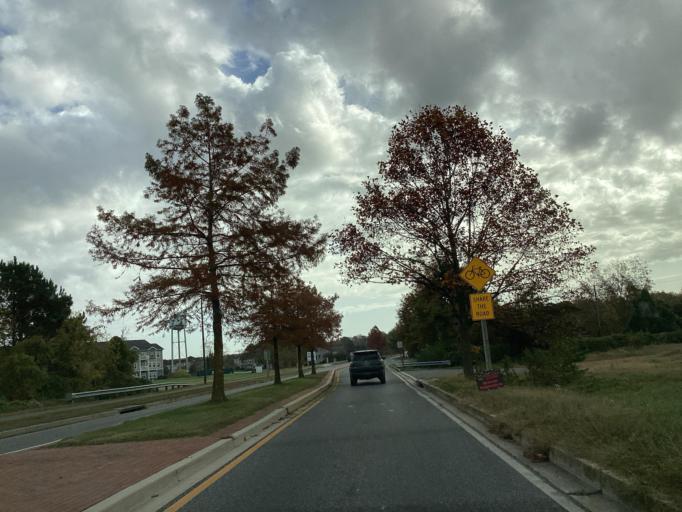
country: US
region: Maryland
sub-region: Somerset County
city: Princess Anne
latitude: 38.2191
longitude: -75.6951
